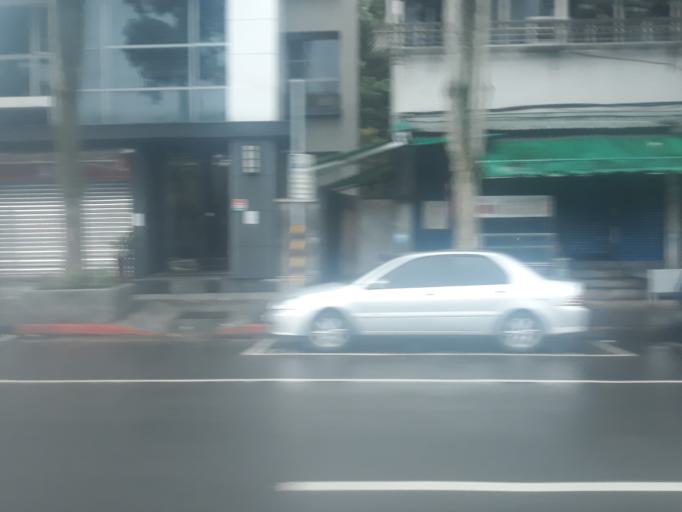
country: TW
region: Taipei
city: Taipei
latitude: 24.9934
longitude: 121.5739
